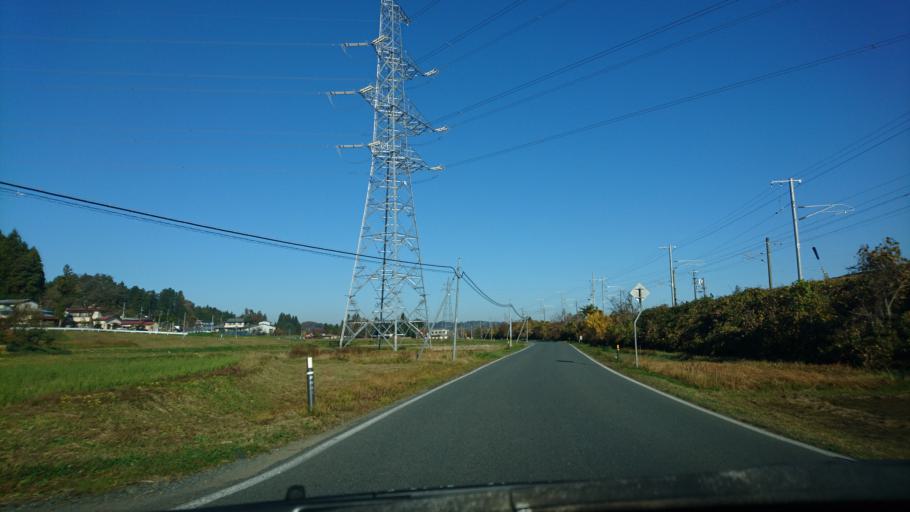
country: JP
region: Iwate
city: Ichinoseki
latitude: 39.0249
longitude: 141.1295
